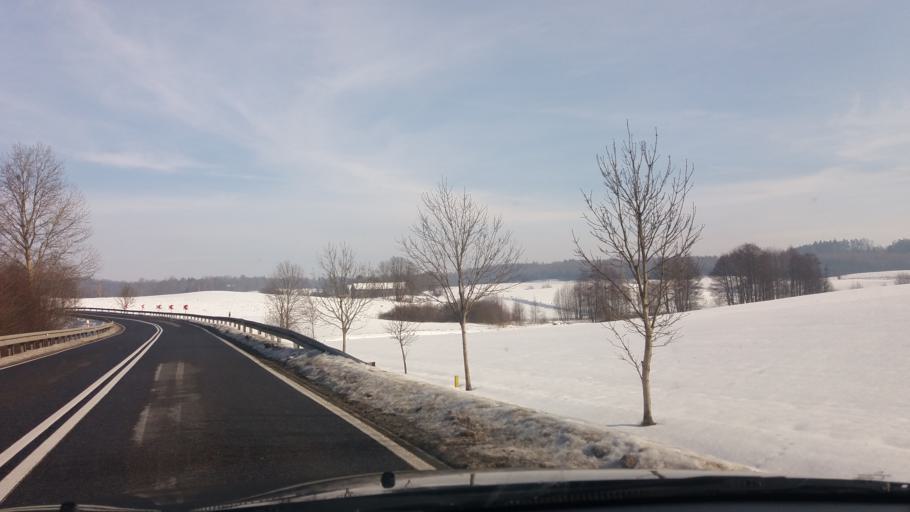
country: PL
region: Warmian-Masurian Voivodeship
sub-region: Powiat olsztynski
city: Czerwonka
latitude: 53.9405
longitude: 20.8882
